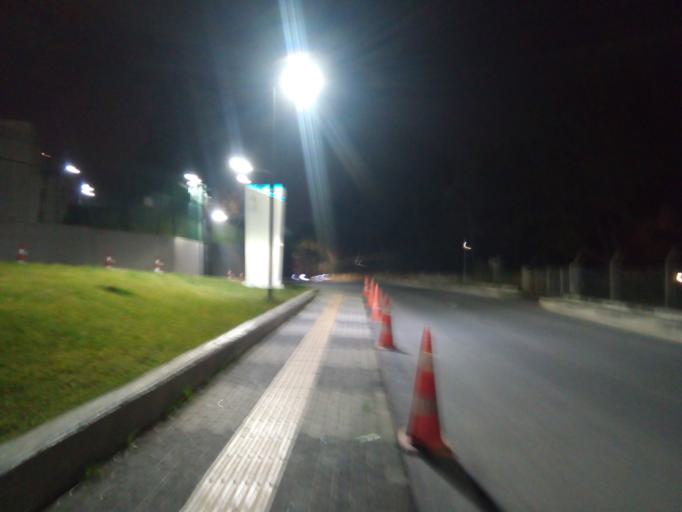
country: TR
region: Istanbul
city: Sisli
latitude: 41.1111
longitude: 29.0391
